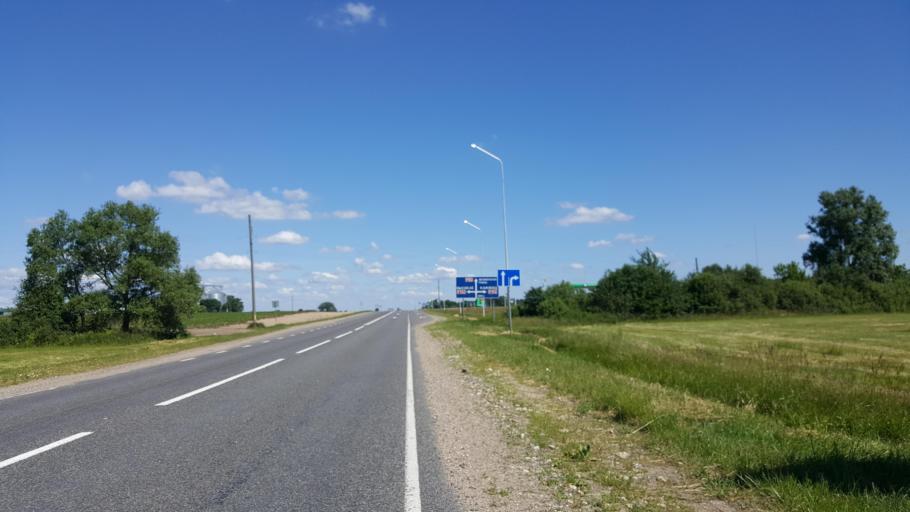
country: BY
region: Brest
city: Kamyanyets
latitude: 52.3955
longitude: 23.7857
